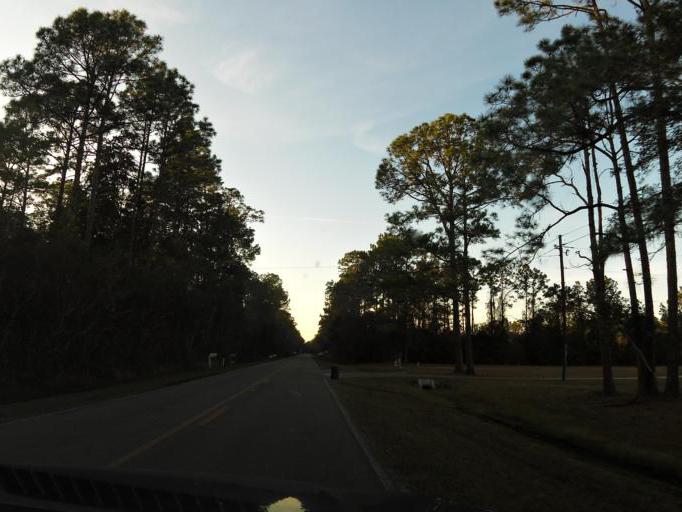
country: US
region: Florida
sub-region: Clay County
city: Green Cove Springs
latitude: 29.8933
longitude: -81.5710
